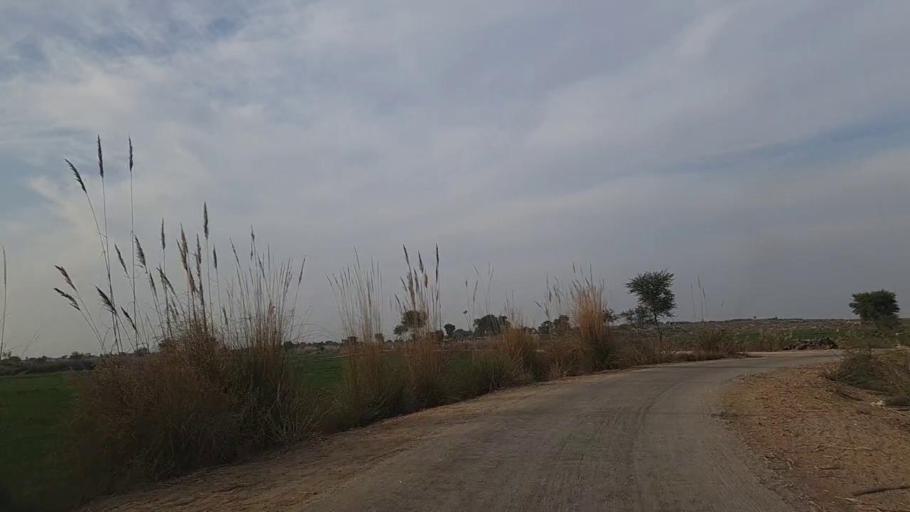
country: PK
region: Sindh
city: Daur
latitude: 26.5033
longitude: 68.4406
